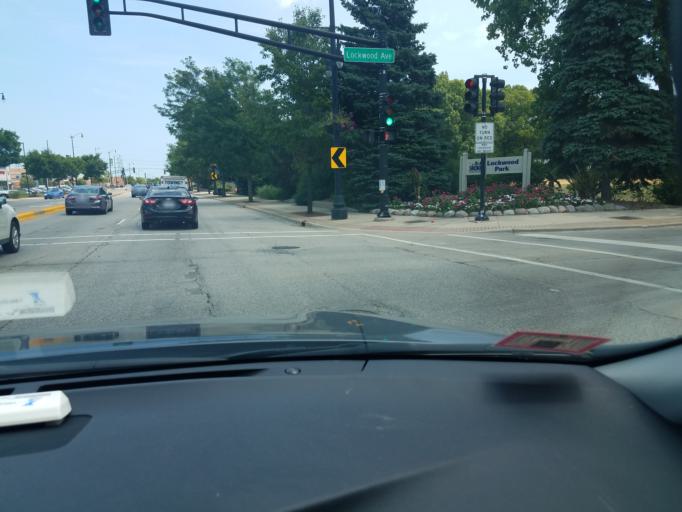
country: US
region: Illinois
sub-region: Cook County
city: Morton Grove
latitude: 42.0408
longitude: -87.7593
